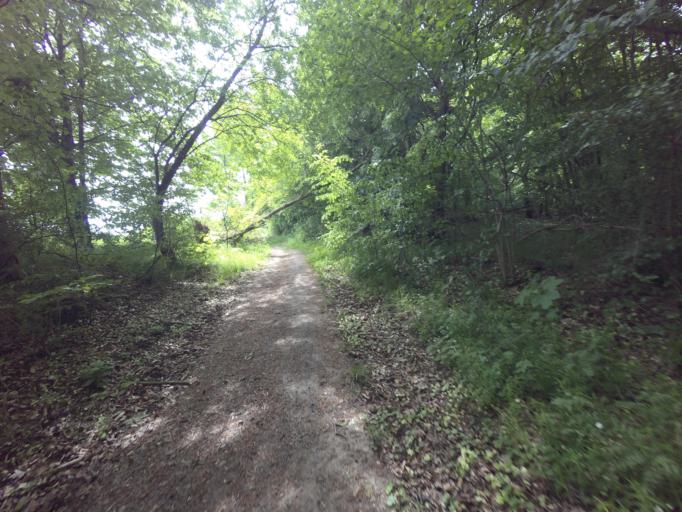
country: DE
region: Lower Saxony
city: Erkerode
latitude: 52.2066
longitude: 10.7488
